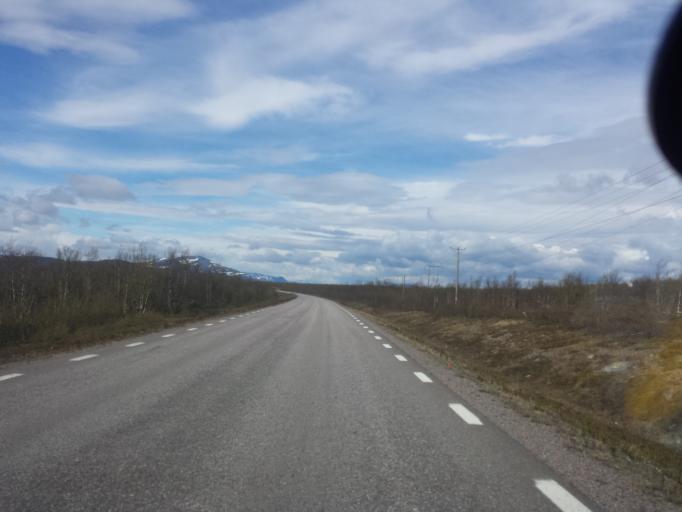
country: SE
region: Norrbotten
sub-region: Kiruna Kommun
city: Kiruna
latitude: 68.0487
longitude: 19.8305
